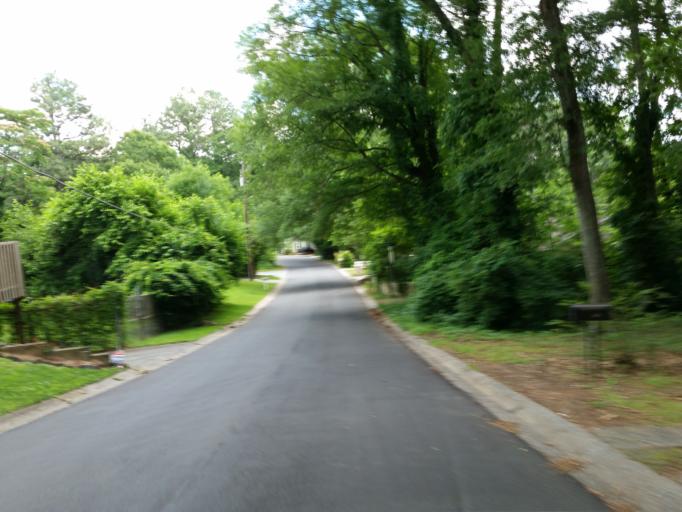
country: US
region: Georgia
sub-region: Cobb County
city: Marietta
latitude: 33.9553
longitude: -84.5313
